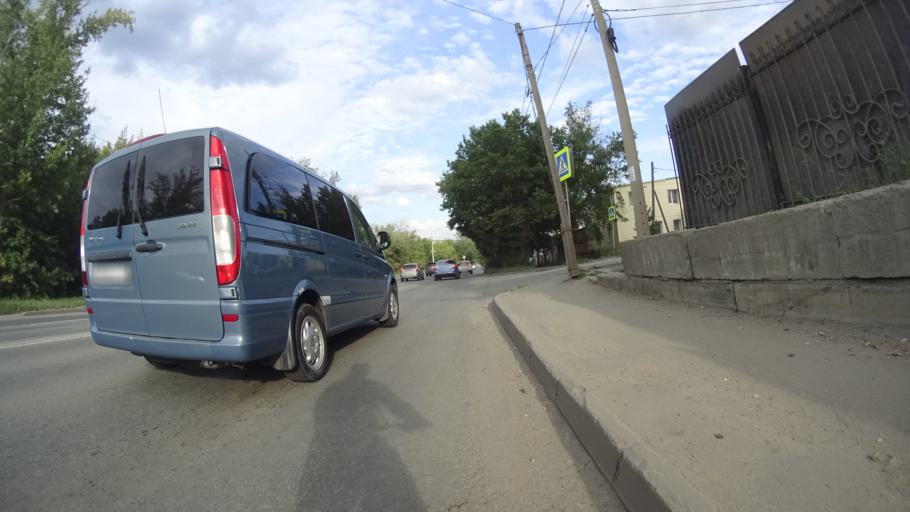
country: RU
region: Chelyabinsk
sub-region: Gorod Chelyabinsk
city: Chelyabinsk
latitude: 55.1984
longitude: 61.3646
